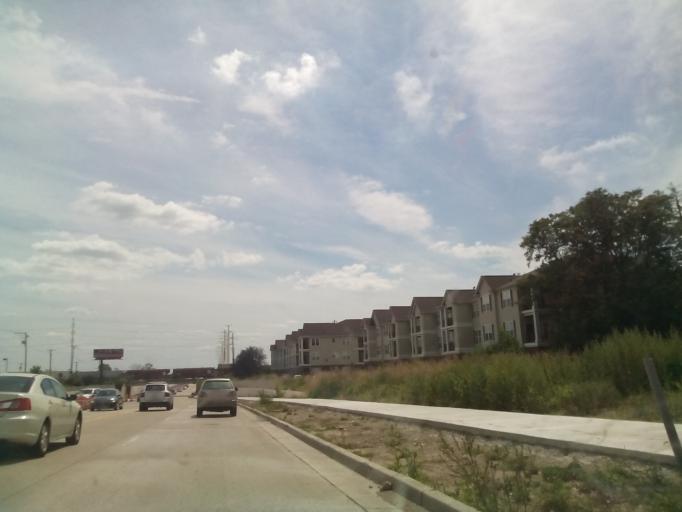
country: US
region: Illinois
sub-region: DuPage County
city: Warrenville
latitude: 41.7805
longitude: -88.2059
